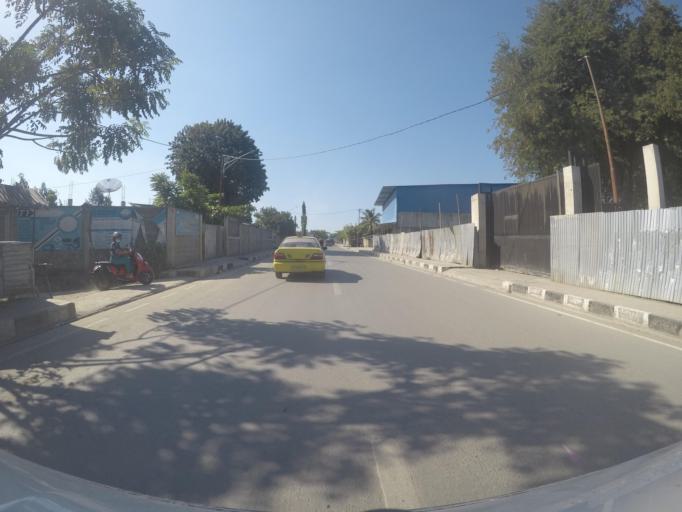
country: TL
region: Dili
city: Dili
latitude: -8.5635
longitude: 125.5559
